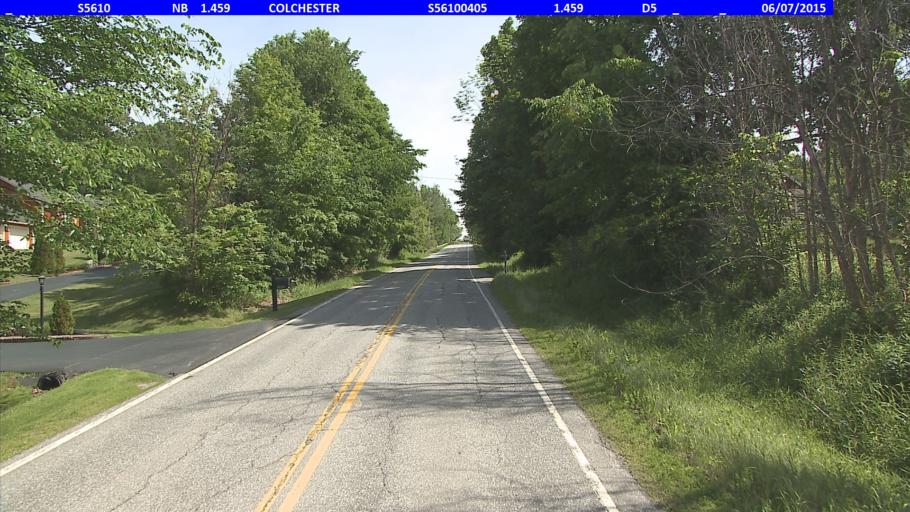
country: US
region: Vermont
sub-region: Chittenden County
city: Colchester
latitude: 44.5614
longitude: -73.1329
